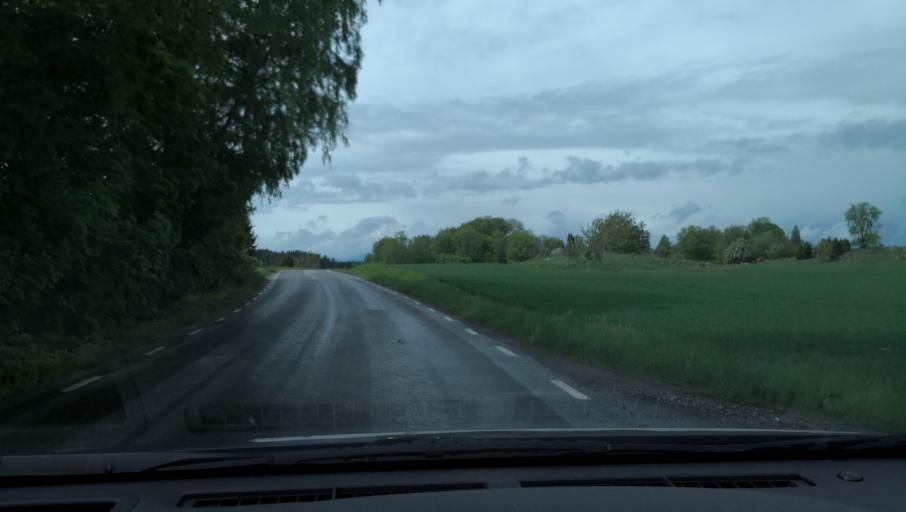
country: SE
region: Uppsala
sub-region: Enkopings Kommun
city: Orsundsbro
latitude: 59.6989
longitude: 17.3666
